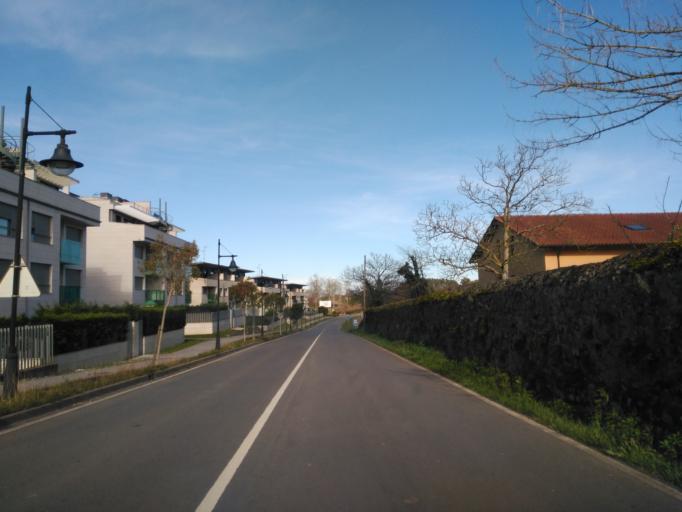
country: ES
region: Asturias
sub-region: Province of Asturias
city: Llanes
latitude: 43.4078
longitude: -4.7582
